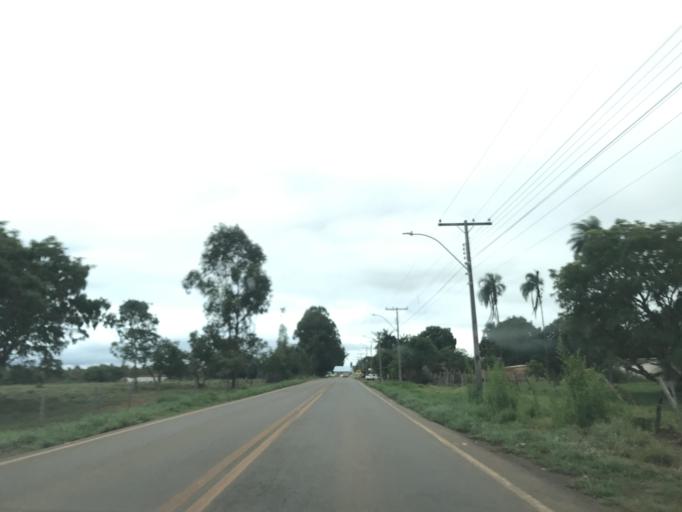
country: BR
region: Goias
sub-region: Luziania
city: Luziania
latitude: -16.3157
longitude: -48.0160
